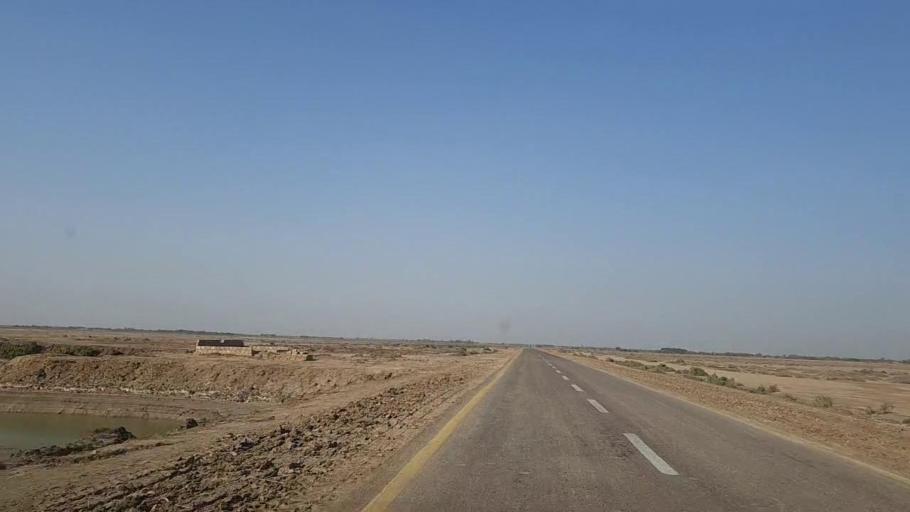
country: PK
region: Sindh
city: Jati
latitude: 24.4969
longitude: 68.3765
